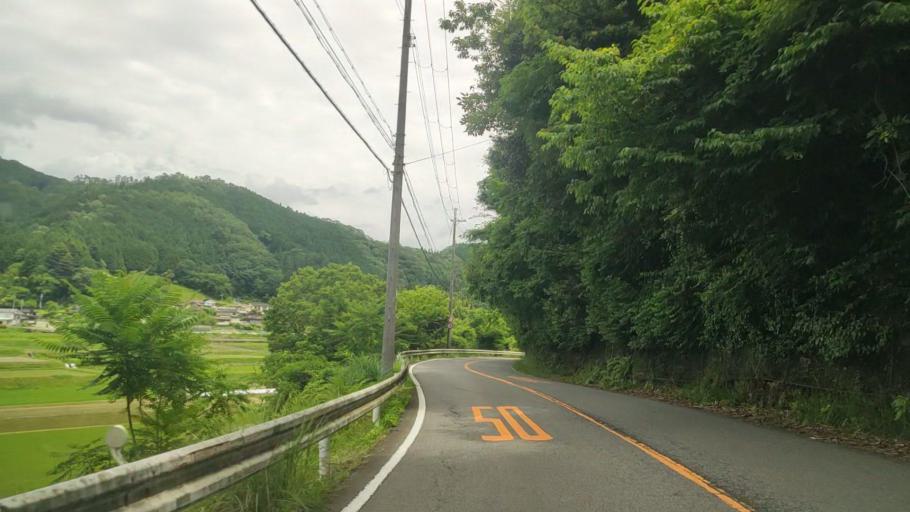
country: JP
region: Hyogo
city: Yamazakicho-nakabirose
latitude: 35.1045
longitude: 134.3606
